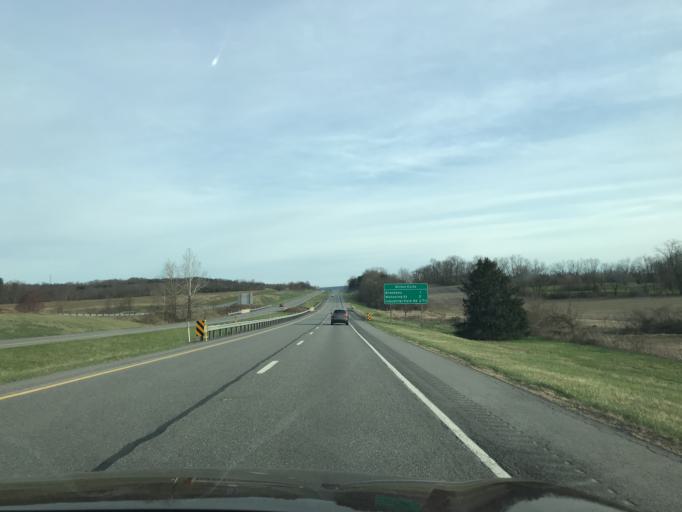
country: US
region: Pennsylvania
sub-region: Union County
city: New Columbia
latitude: 41.0404
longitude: -76.8412
